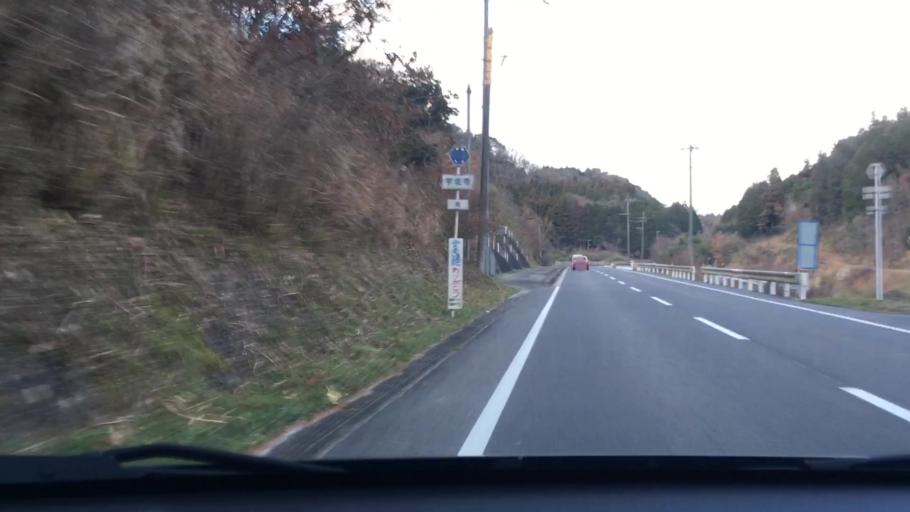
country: JP
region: Oita
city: Bungo-Takada-shi
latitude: 33.4712
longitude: 131.3846
